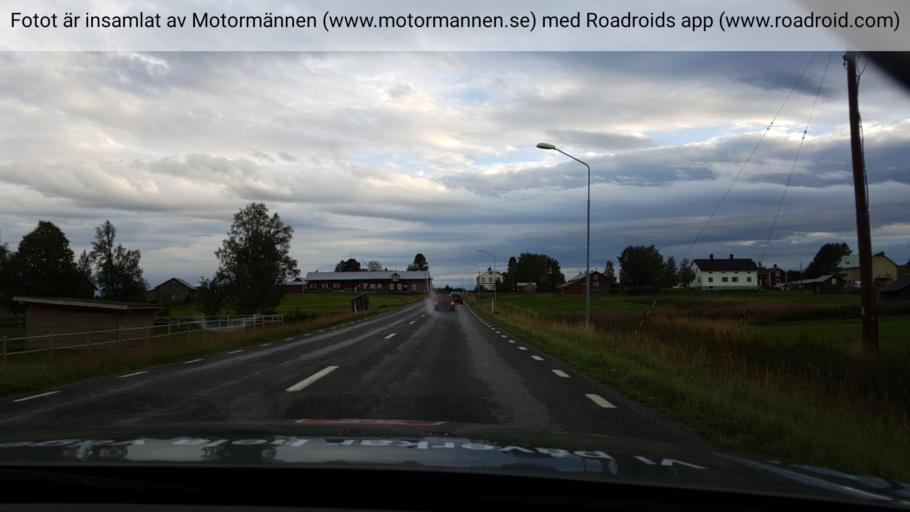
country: SE
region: Jaemtland
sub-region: Stroemsunds Kommun
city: Stroemsund
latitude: 63.4997
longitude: 15.2593
